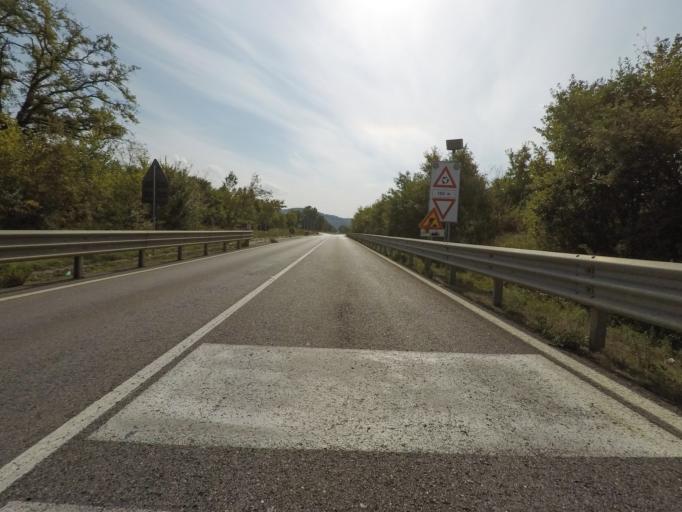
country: IT
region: Tuscany
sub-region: Provincia di Siena
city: Rosia
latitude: 43.2214
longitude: 11.2741
